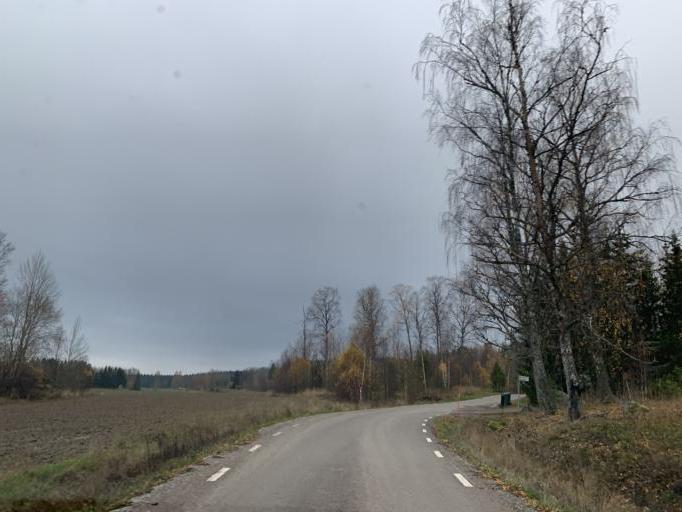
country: SE
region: Vaestmanland
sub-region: Surahammars Kommun
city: Ramnas
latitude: 59.7441
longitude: 16.1725
